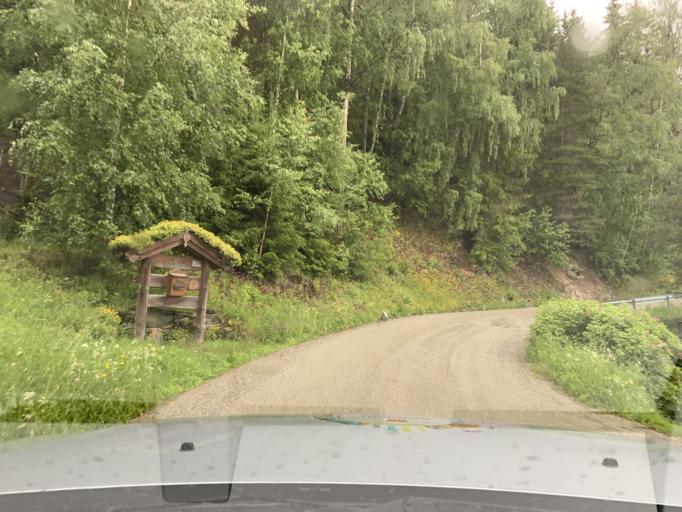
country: NO
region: Oppland
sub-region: Oyer
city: Tretten
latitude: 61.3914
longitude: 10.2501
